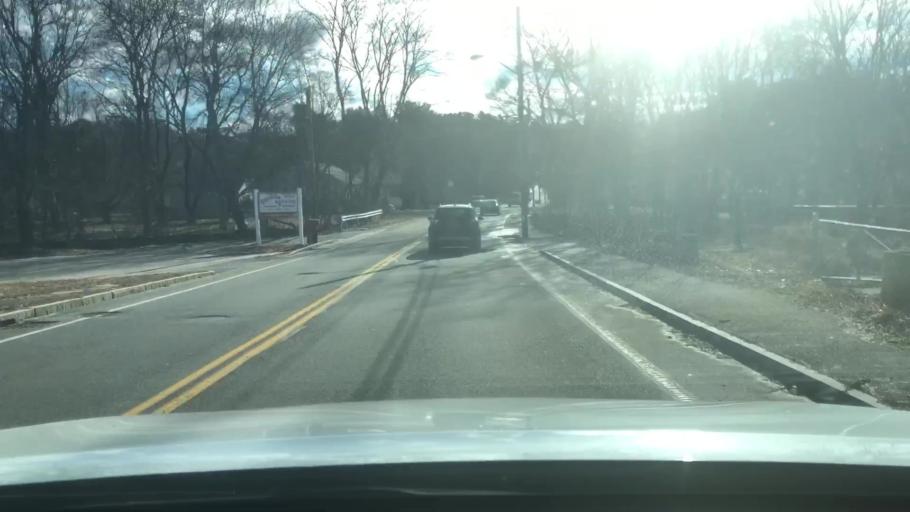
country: US
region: Rhode Island
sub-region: Providence County
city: Woonsocket
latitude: 42.0246
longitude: -71.4878
